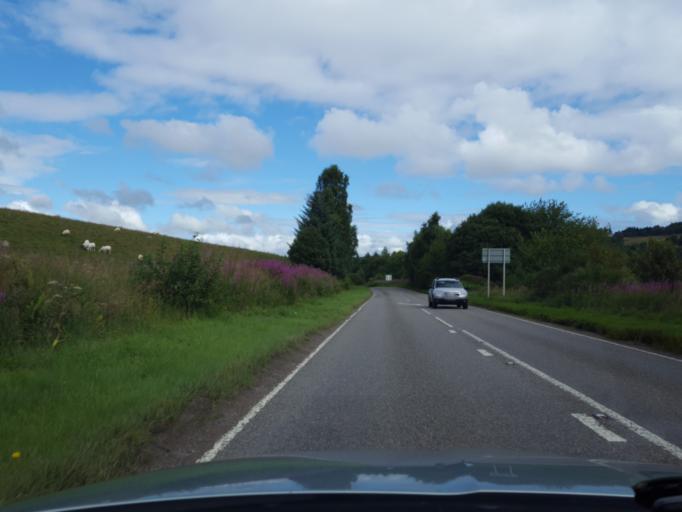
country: GB
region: Scotland
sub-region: Moray
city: Rothes
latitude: 57.5004
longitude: -3.1926
